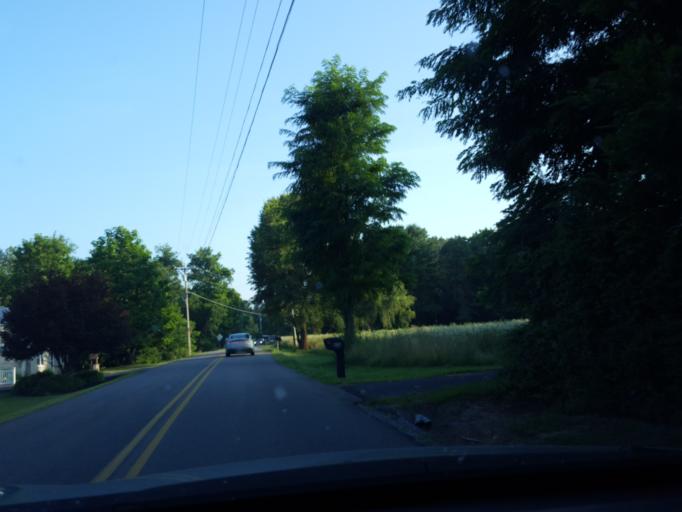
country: US
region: Virginia
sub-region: Augusta County
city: Lyndhurst
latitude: 37.9743
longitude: -78.9569
